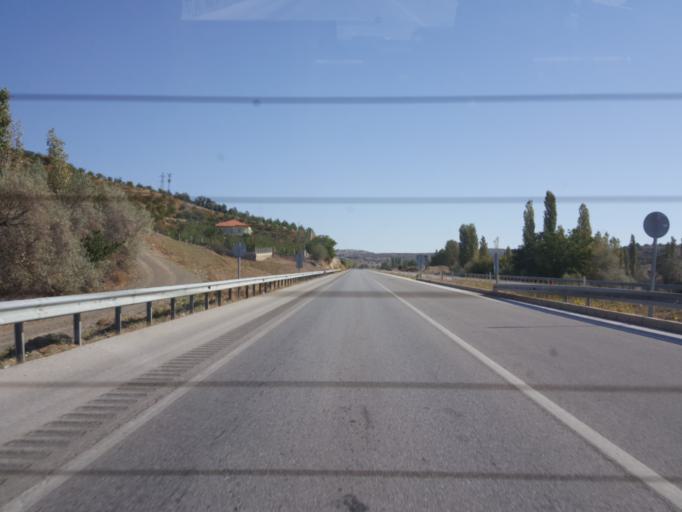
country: TR
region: Corum
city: Alaca
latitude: 40.2607
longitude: 34.6263
